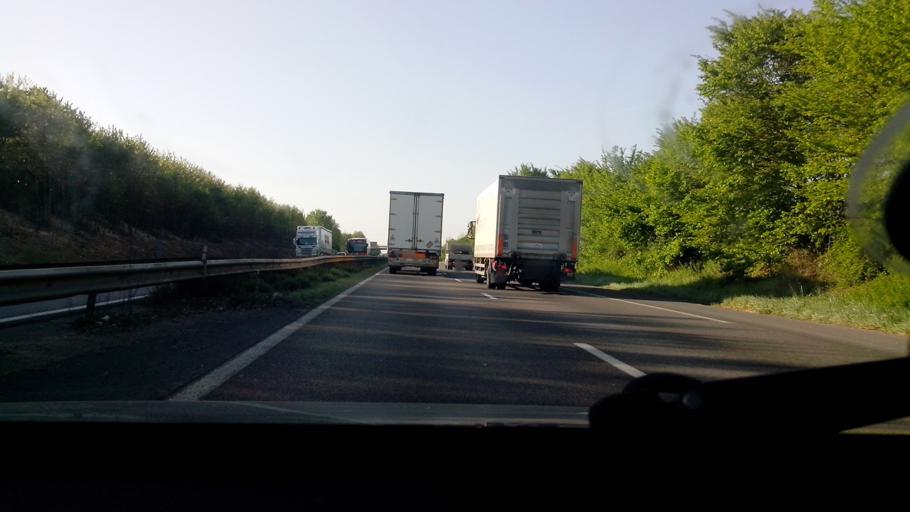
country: FR
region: Ile-de-France
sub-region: Departement de Seine-et-Marne
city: Servon
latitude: 48.6967
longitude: 2.5943
